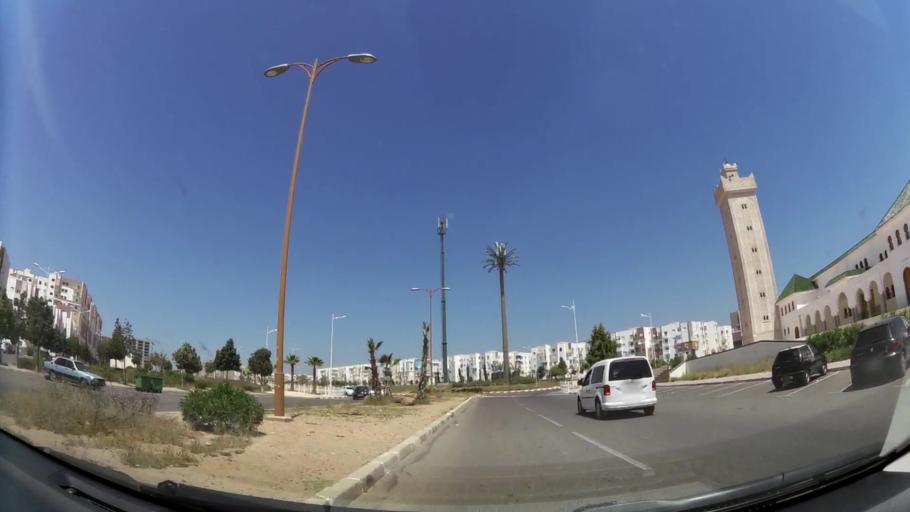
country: MA
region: Oued ed Dahab-Lagouira
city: Dakhla
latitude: 30.4334
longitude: -9.5570
